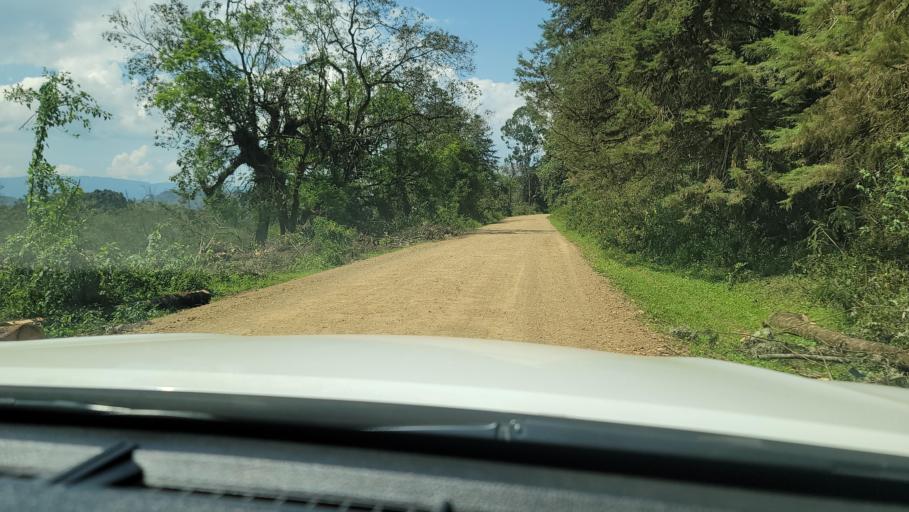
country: ET
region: Oromiya
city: Agaro
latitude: 7.7889
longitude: 36.4299
